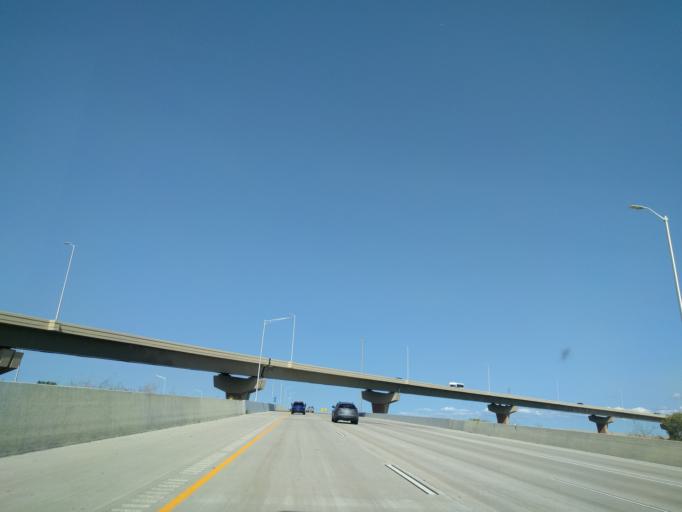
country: US
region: Wisconsin
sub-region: Brown County
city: Howard
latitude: 44.5601
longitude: -88.0549
